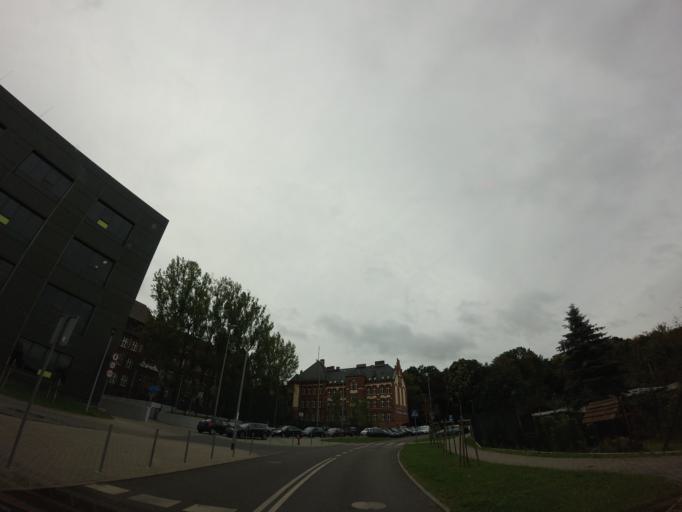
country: PL
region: West Pomeranian Voivodeship
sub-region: Szczecin
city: Szczecin
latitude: 53.4501
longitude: 14.5356
